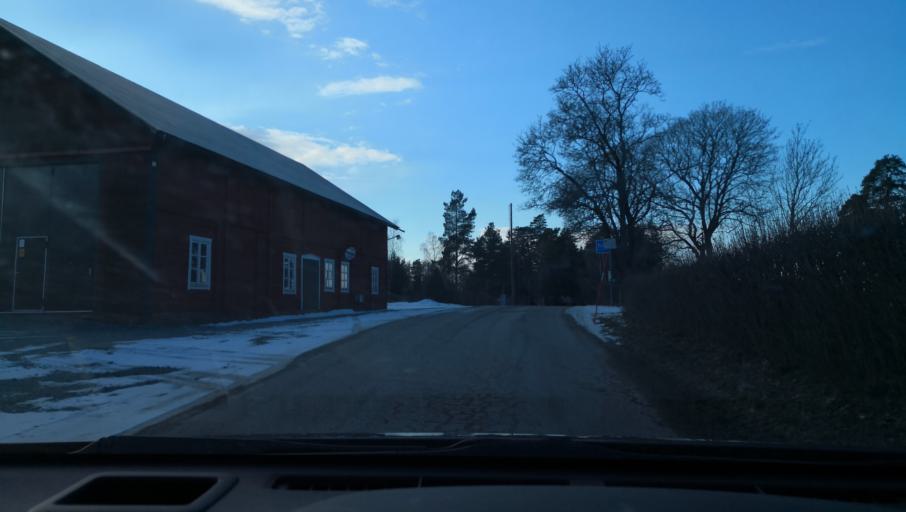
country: SE
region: Uppsala
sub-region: Enkopings Kommun
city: Irsta
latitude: 59.6586
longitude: 16.7905
